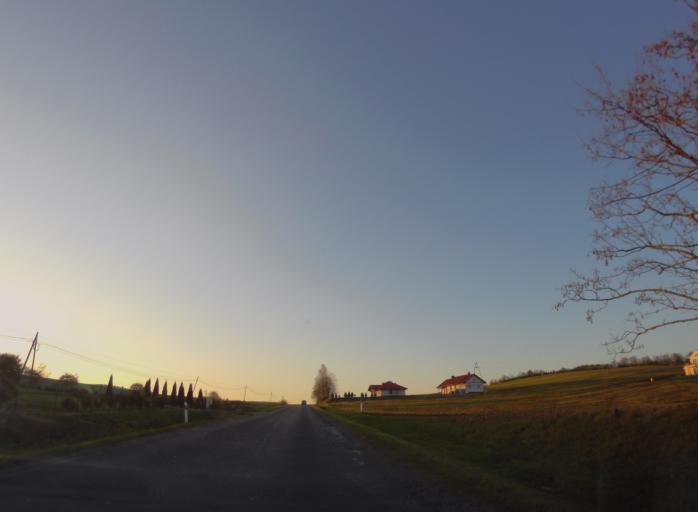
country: PL
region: Subcarpathian Voivodeship
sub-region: Powiat leski
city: Lesko
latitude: 49.4184
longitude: 22.3350
